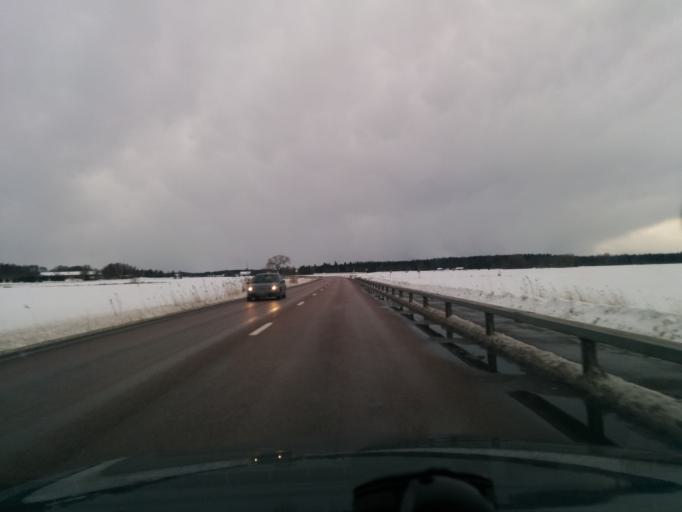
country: SE
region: Vaestmanland
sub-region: Vasteras
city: Skultuna
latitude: 59.5826
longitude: 16.4157
